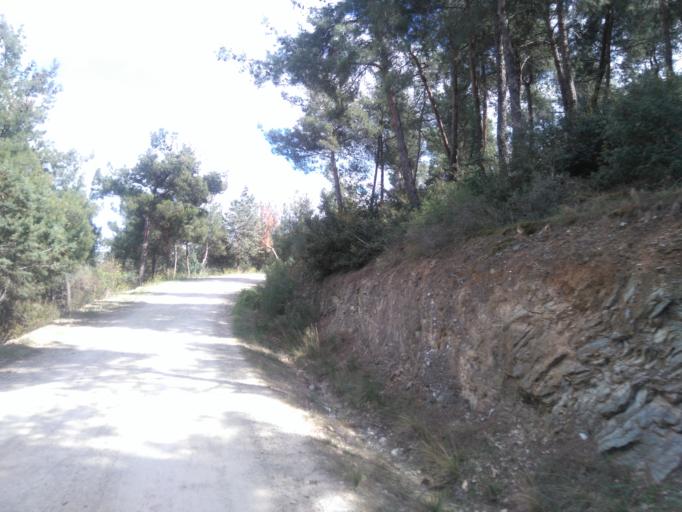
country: GR
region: Central Macedonia
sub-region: Nomos Thessalonikis
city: Agios Pavlos
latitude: 40.6585
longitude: 22.9720
